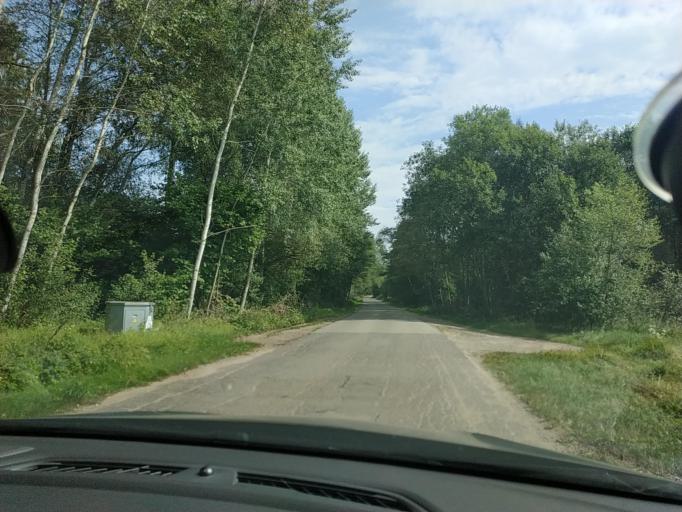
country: LT
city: Nemencine
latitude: 54.8472
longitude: 25.4553
